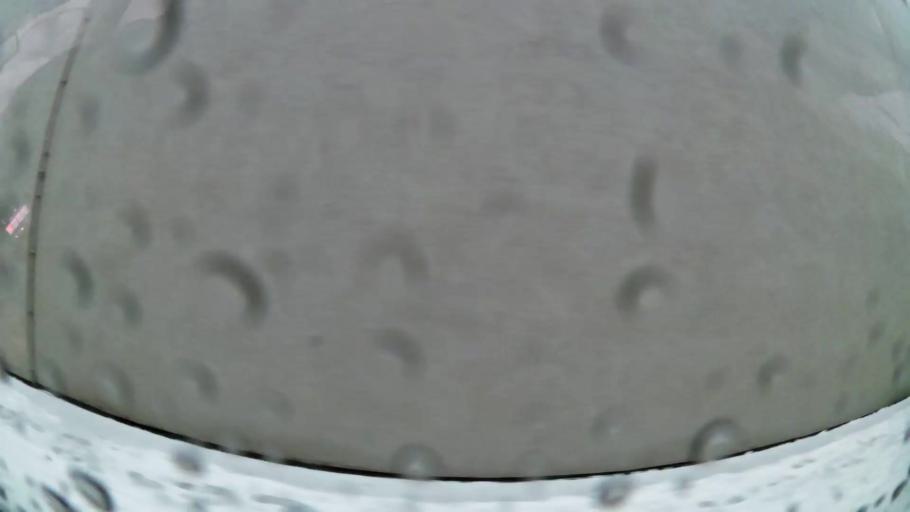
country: RS
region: Central Serbia
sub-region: Belgrade
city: Zemun
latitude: 44.8119
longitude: 20.3921
